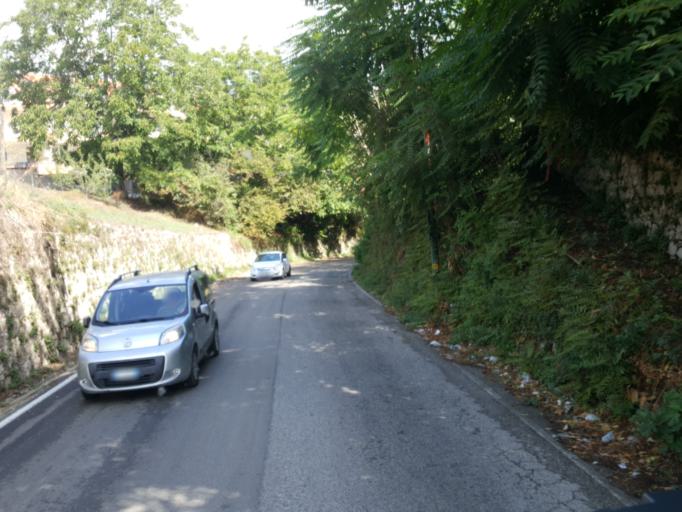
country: IT
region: Campania
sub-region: Provincia di Avellino
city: Domicella
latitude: 40.8820
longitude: 14.5897
